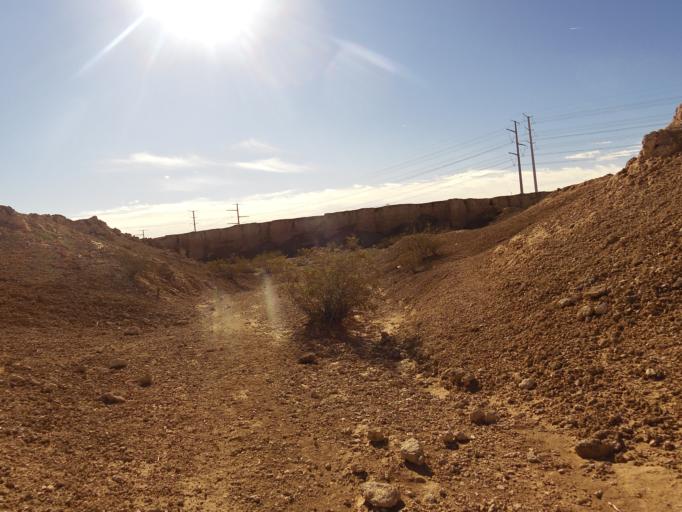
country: US
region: Nevada
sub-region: Clark County
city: North Las Vegas
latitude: 36.3375
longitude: -115.2755
